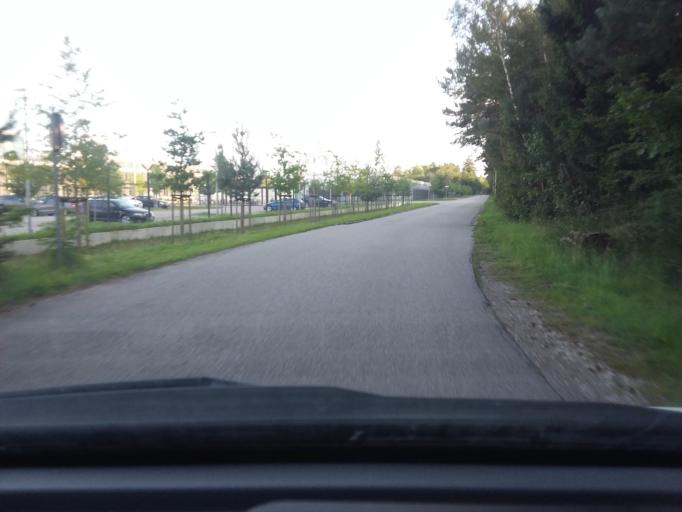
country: DE
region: Bavaria
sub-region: Upper Bavaria
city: Oberschleissheim
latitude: 48.2323
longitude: 11.5633
